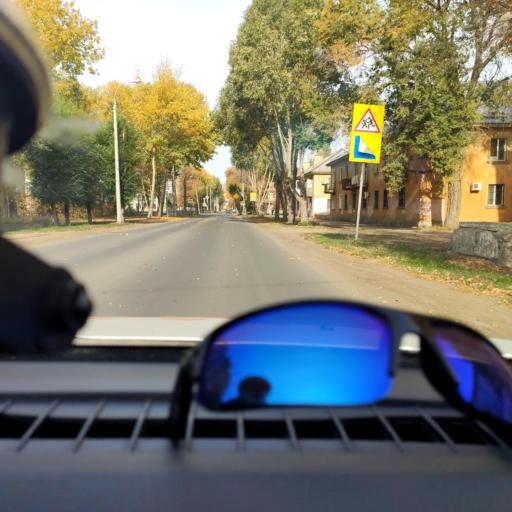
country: RU
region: Samara
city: Samara
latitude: 53.1127
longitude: 50.0740
